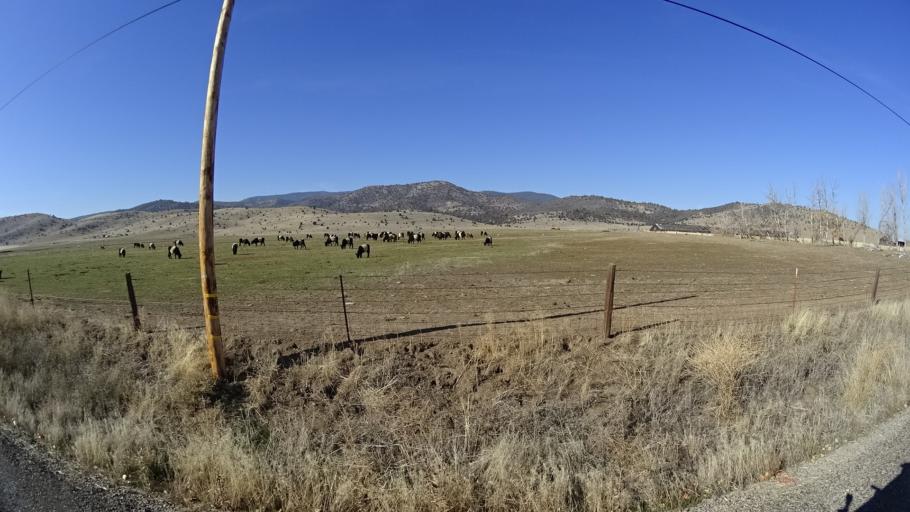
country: US
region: California
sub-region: Siskiyou County
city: Montague
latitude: 41.6173
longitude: -122.5300
